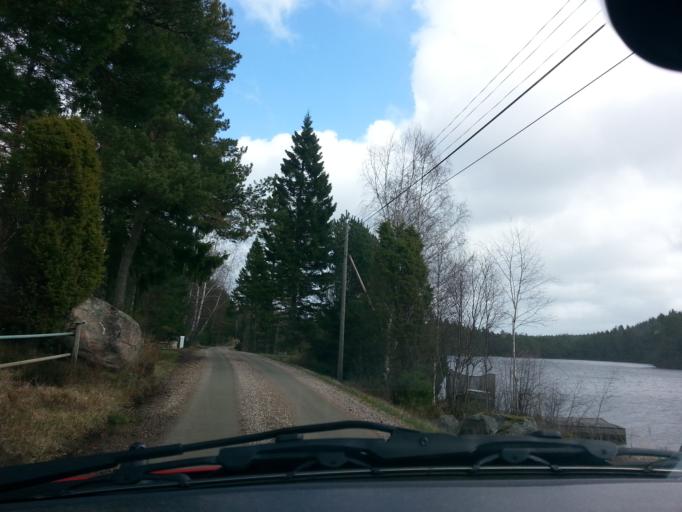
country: SE
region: Vaestra Goetaland
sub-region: Lerums Kommun
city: Grabo
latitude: 57.8872
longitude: 12.2876
